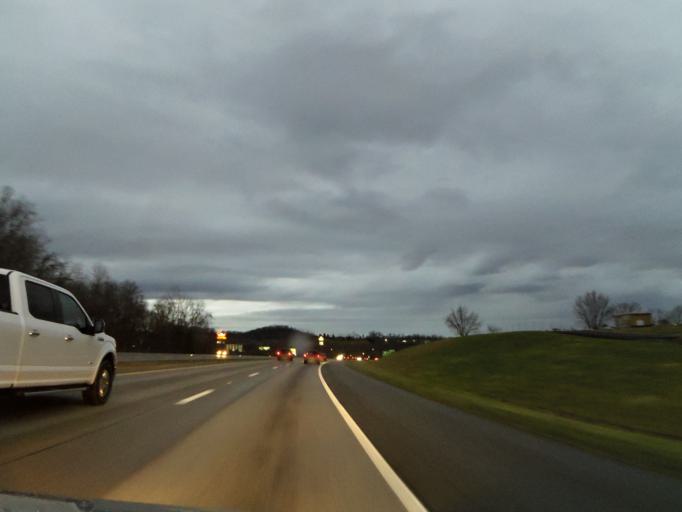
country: US
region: Tennessee
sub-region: Washington County
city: Oak Grove
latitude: 36.3727
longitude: -82.4227
